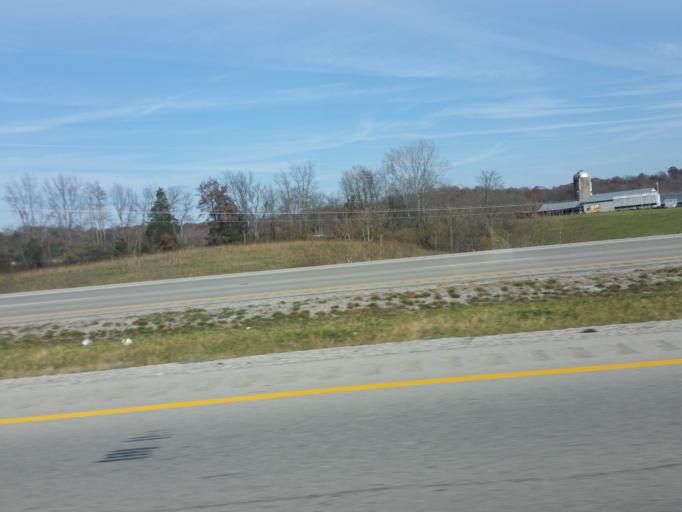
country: US
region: Kentucky
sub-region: Campbell County
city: Claryville
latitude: 38.8553
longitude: -84.3851
